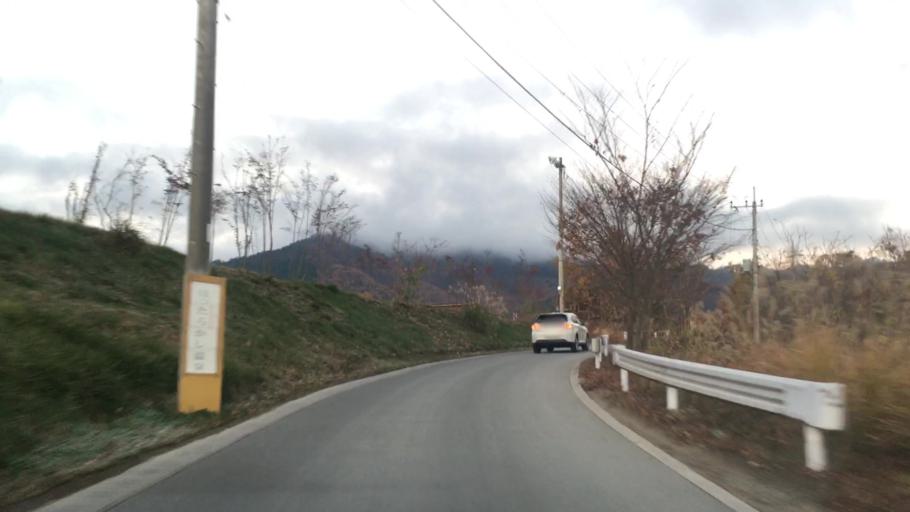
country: JP
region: Yamanashi
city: Isawa
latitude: 35.7075
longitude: 138.6515
